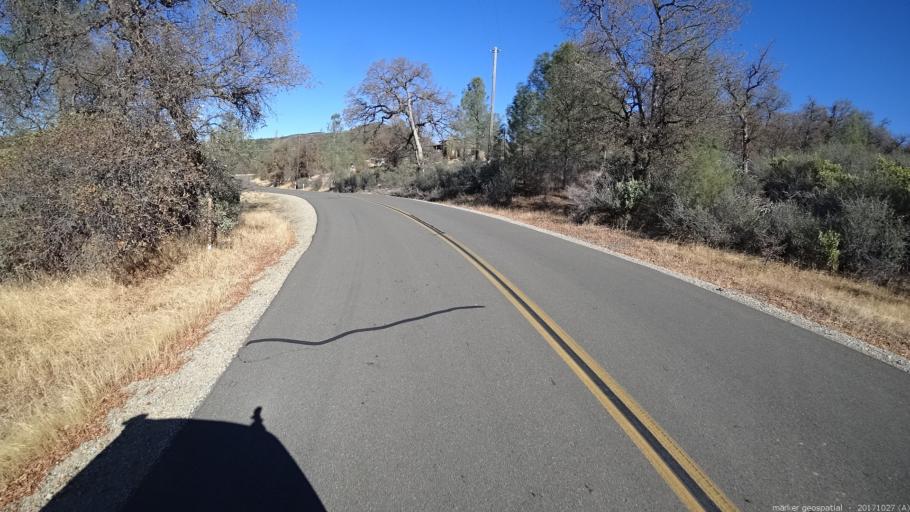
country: US
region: California
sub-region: Shasta County
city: Shingletown
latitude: 40.7762
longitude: -121.9588
